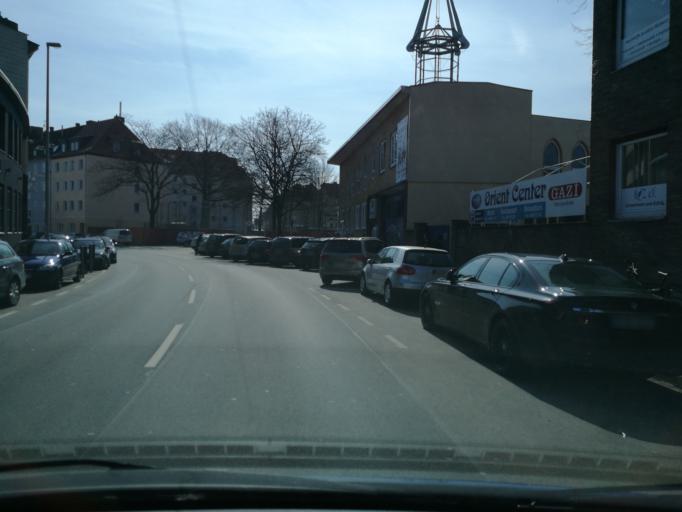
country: DE
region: Lower Saxony
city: Hannover
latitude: 52.3845
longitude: 9.7295
